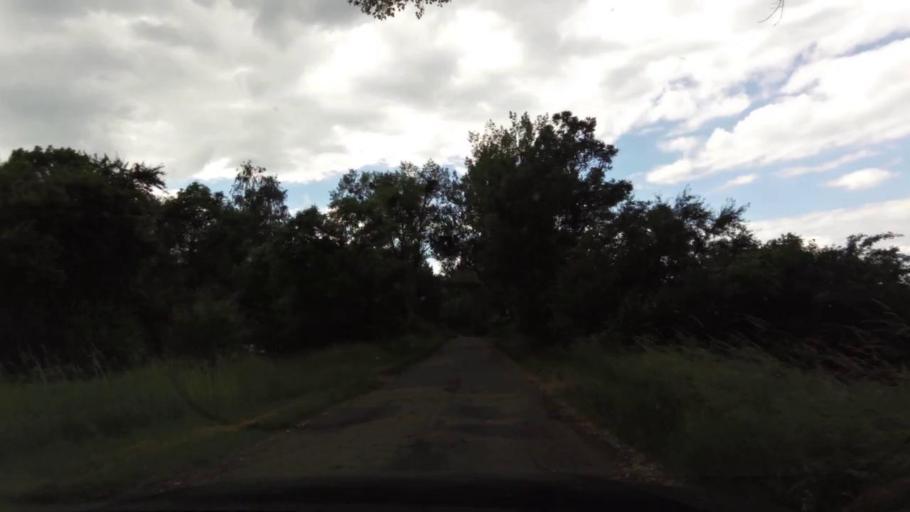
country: PL
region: West Pomeranian Voivodeship
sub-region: Powiat mysliborski
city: Mysliborz
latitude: 52.9900
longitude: 14.7654
